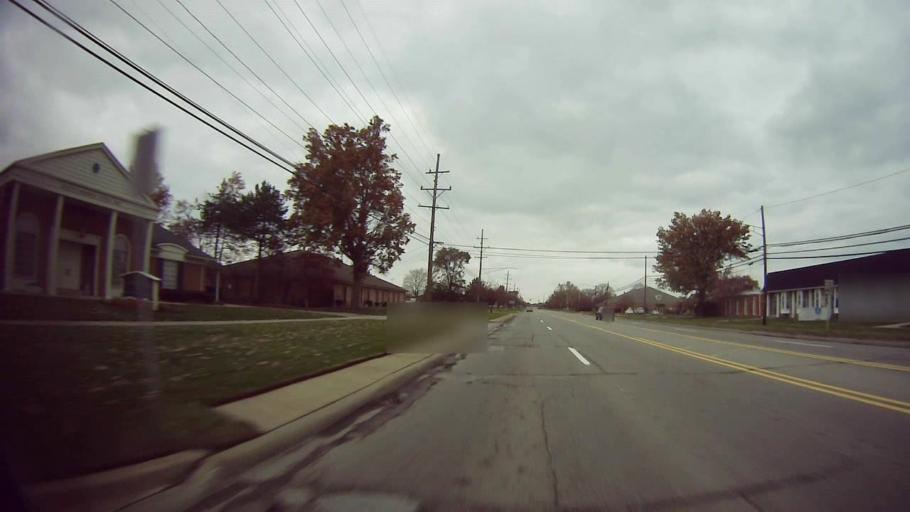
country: US
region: Michigan
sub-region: Macomb County
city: Center Line
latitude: 42.5145
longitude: -83.0073
